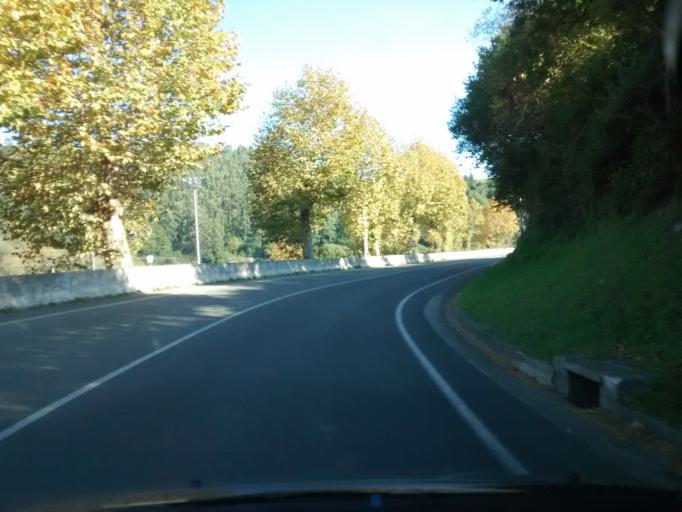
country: ES
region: Basque Country
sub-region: Provincia de Guipuzcoa
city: Deba
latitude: 43.2907
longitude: -2.3665
